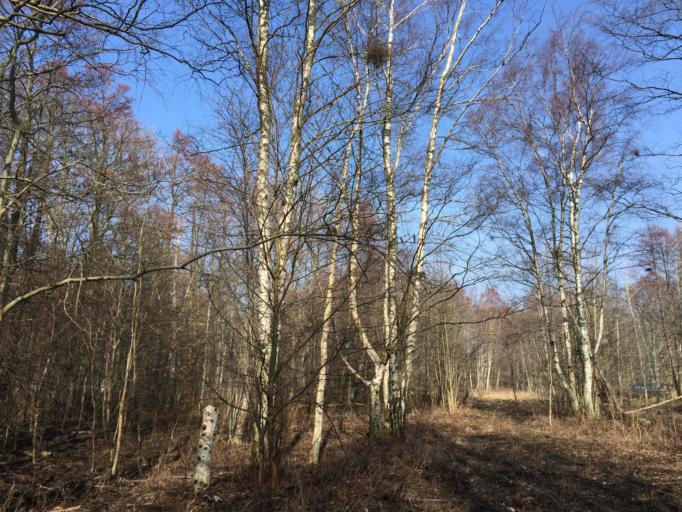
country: LV
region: Dundaga
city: Dundaga
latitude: 57.9333
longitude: 22.0715
